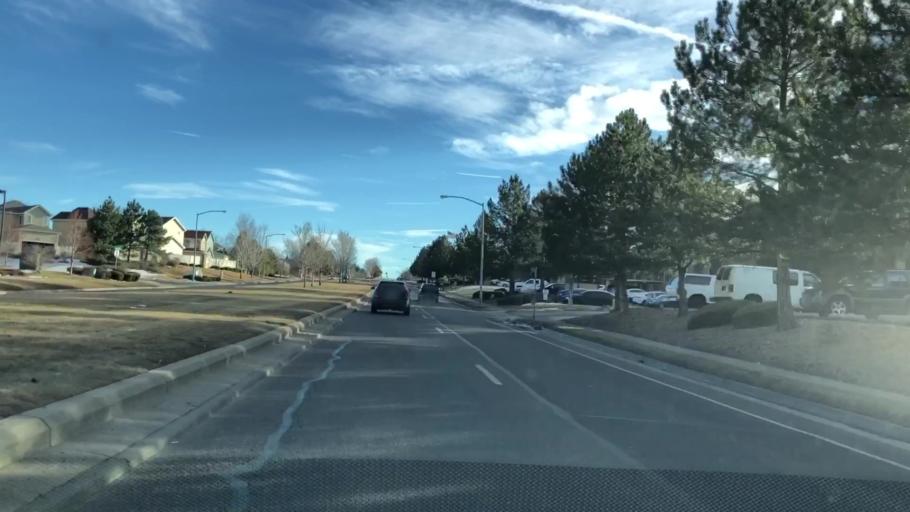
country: US
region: Colorado
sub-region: Adams County
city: Aurora
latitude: 39.6942
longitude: -104.7912
